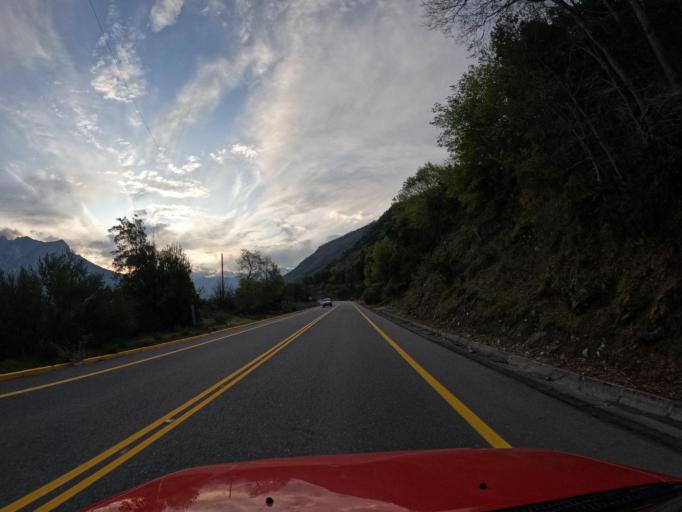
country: CL
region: Maule
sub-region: Provincia de Linares
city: Colbun
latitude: -35.7174
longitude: -71.0353
